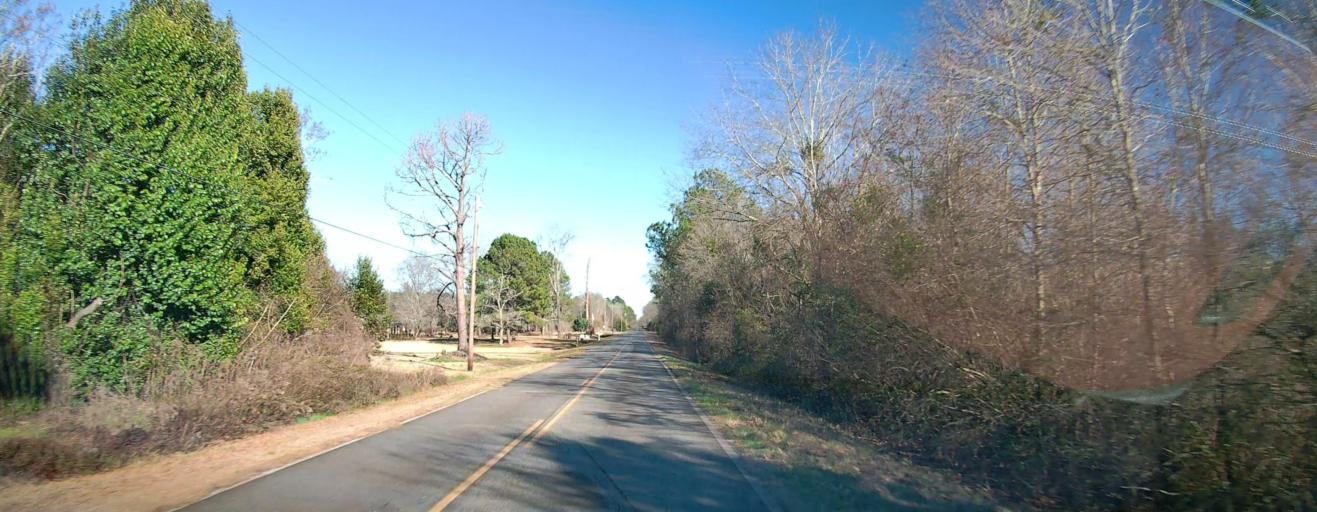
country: US
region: Georgia
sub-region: Sumter County
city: Americus
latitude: 32.0469
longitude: -84.2688
